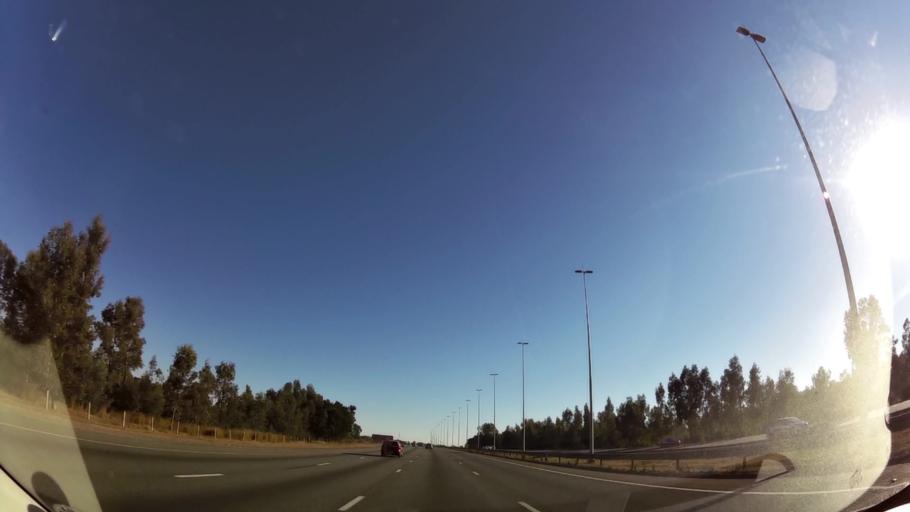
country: ZA
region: Gauteng
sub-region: Ekurhuleni Metropolitan Municipality
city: Tembisa
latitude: -25.9148
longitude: 28.2595
